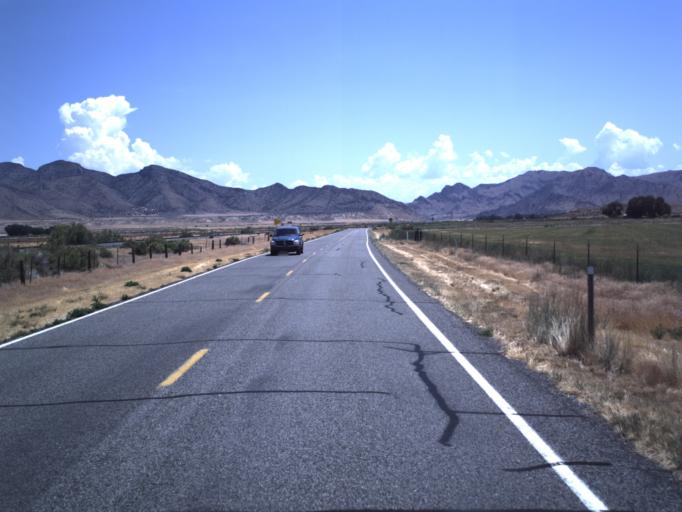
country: US
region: Utah
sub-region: Millard County
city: Delta
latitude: 39.5321
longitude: -112.3331
